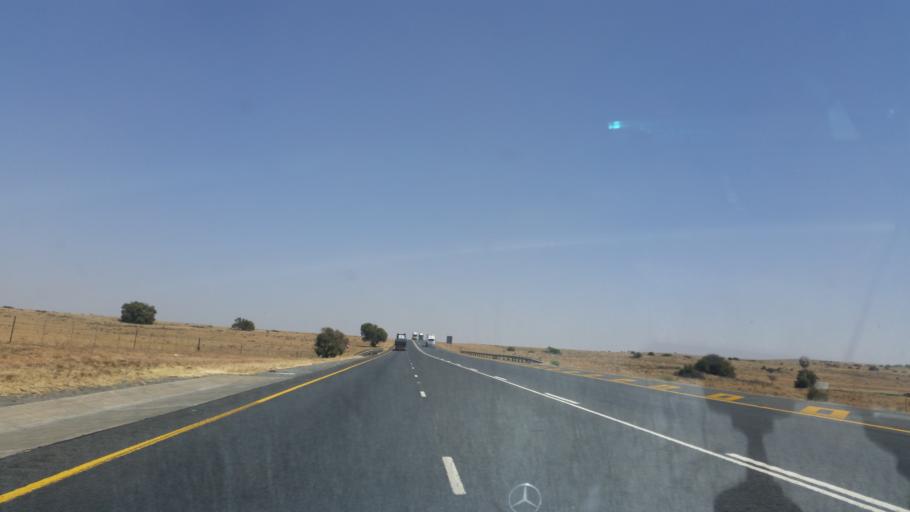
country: ZA
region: Orange Free State
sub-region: Lejweleputswa District Municipality
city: Winburg
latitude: -28.7036
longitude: 26.7946
